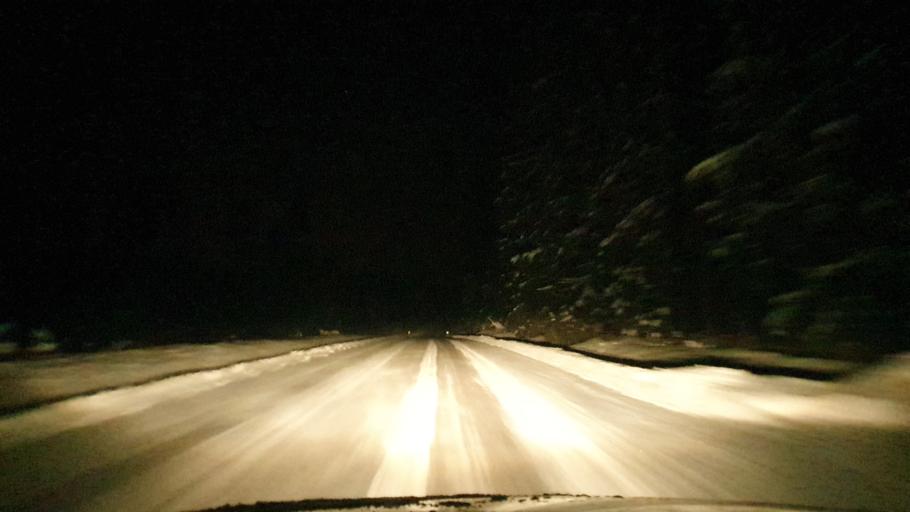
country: EE
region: Vorumaa
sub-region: Antsla vald
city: Vana-Antsla
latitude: 57.9712
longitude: 26.7590
